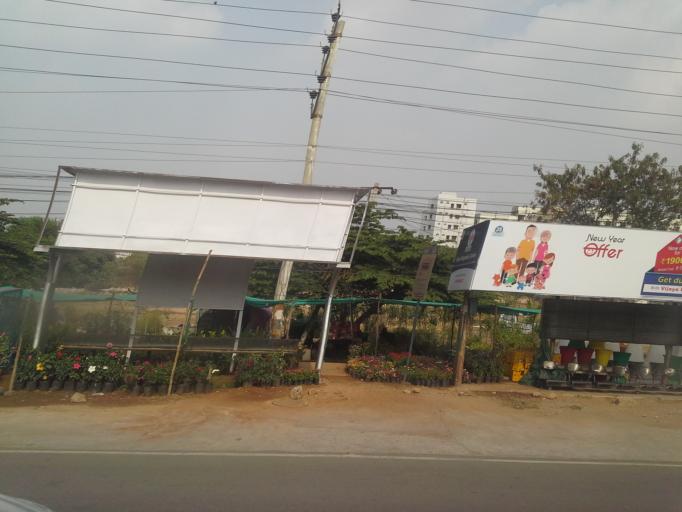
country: IN
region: Telangana
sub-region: Rangareddi
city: Kukatpalli
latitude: 17.4544
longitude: 78.3789
